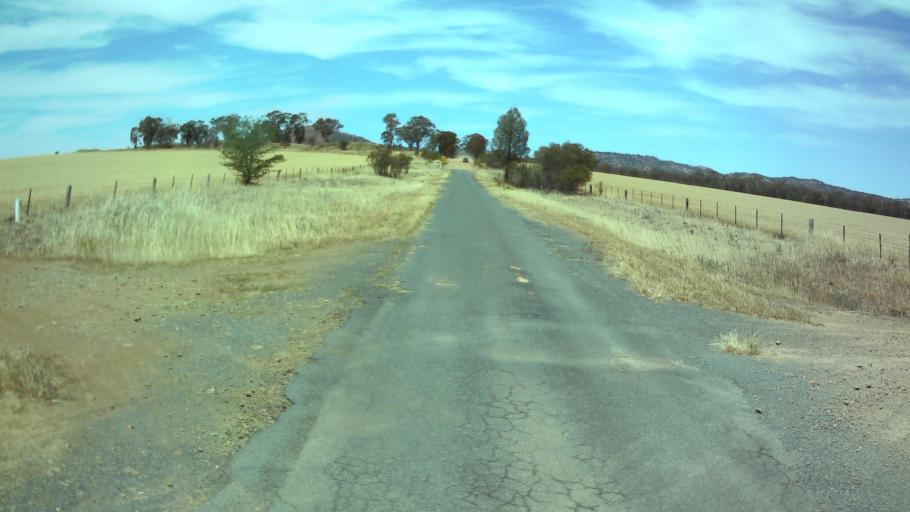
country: AU
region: New South Wales
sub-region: Weddin
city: Grenfell
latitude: -33.7604
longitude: 148.1137
